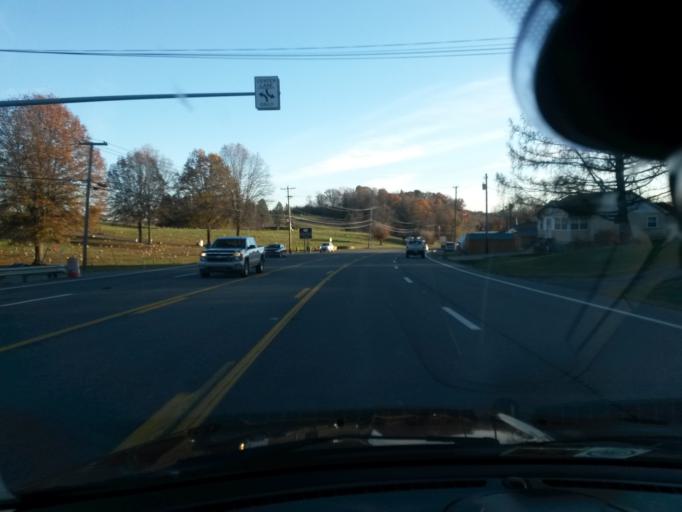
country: US
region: West Virginia
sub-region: Raleigh County
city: Prosperity
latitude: 37.8420
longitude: -81.1935
